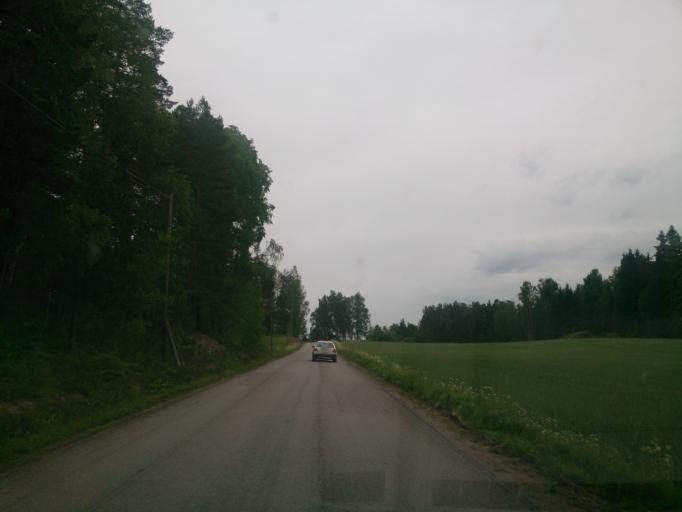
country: SE
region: OEstergoetland
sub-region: Valdemarsviks Kommun
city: Gusum
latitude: 58.3144
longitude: 16.3345
